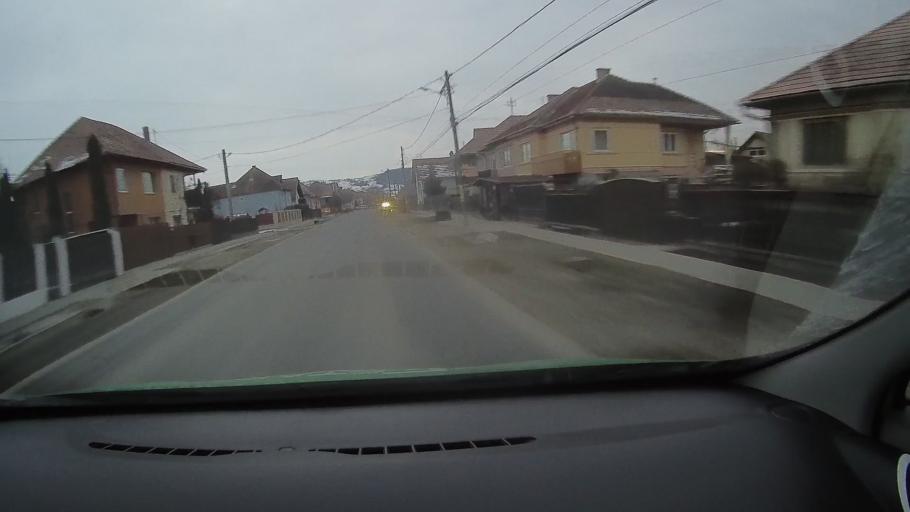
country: RO
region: Harghita
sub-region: Comuna Feliceni
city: Feliceni
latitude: 46.2711
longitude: 25.2758
